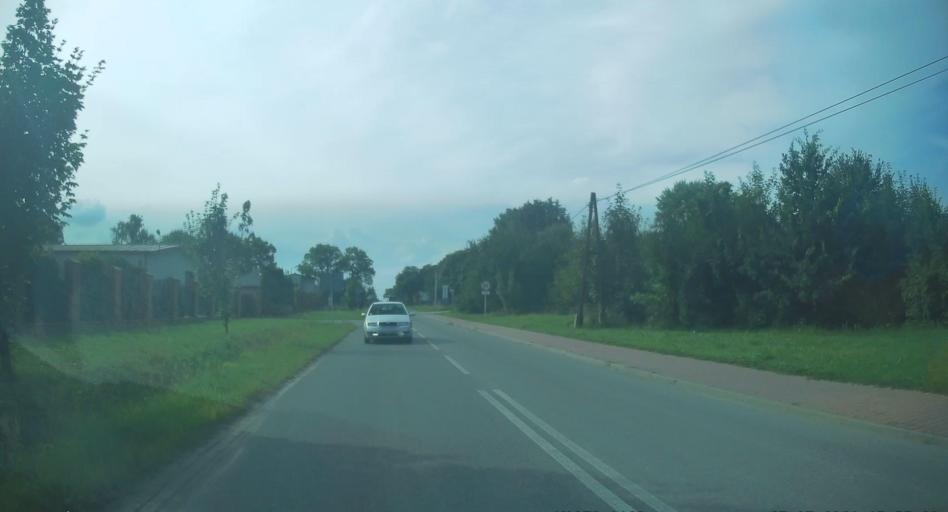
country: PL
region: Lodz Voivodeship
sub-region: Powiat opoczynski
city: Opoczno
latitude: 51.3666
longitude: 20.2987
